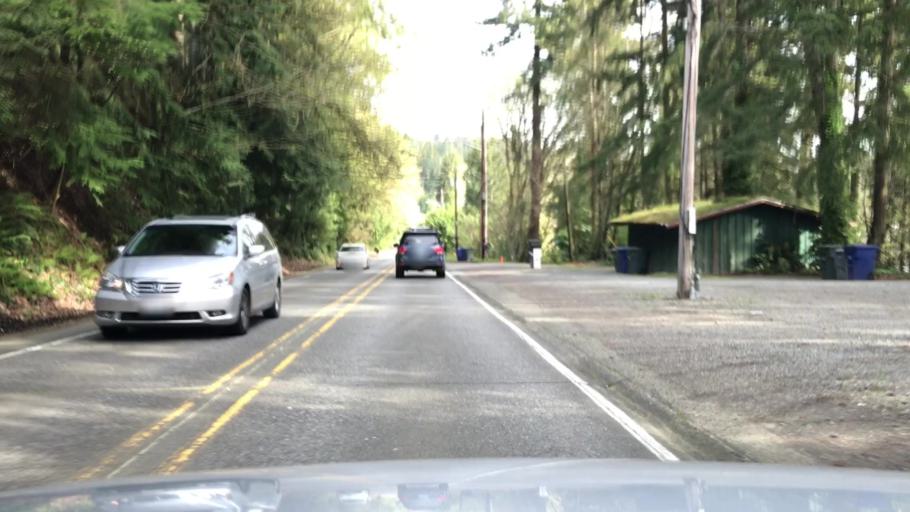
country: US
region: Washington
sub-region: King County
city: West Lake Sammamish
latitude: 47.6019
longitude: -122.1115
